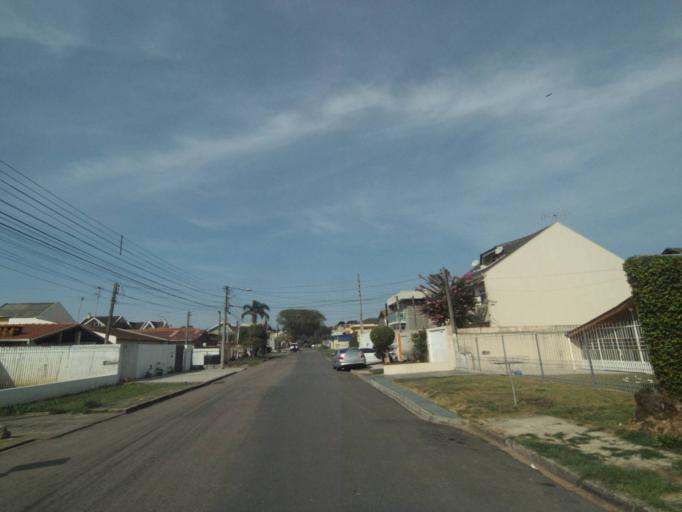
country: BR
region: Parana
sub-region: Curitiba
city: Curitiba
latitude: -25.4615
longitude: -49.3184
